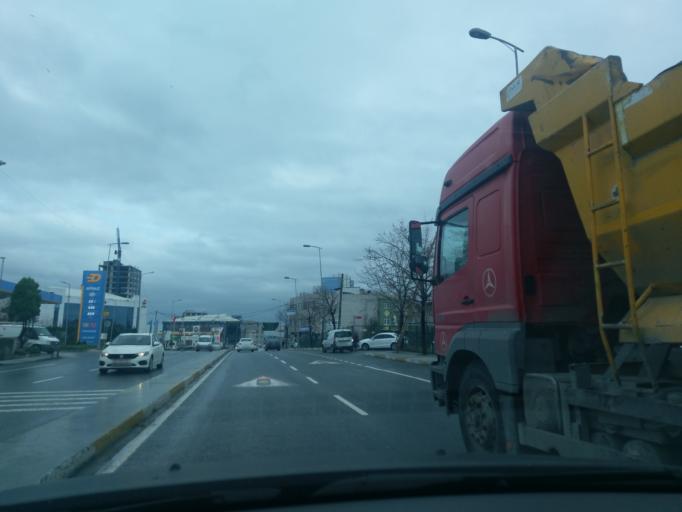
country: TR
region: Istanbul
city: Mahmutbey
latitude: 41.0581
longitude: 28.8311
